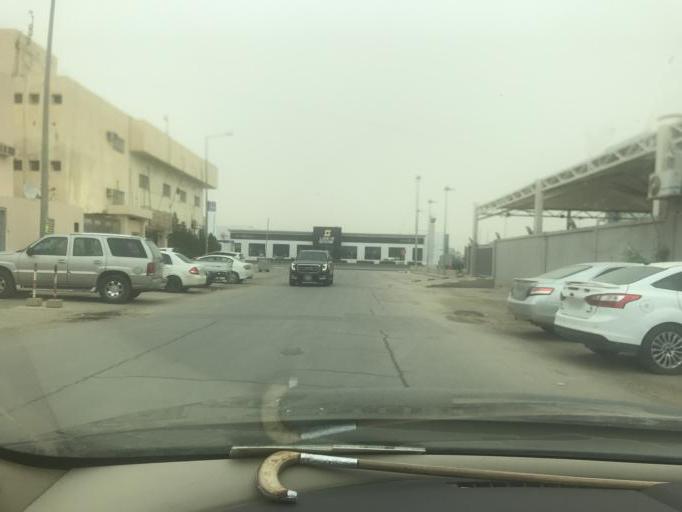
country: SA
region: Ar Riyad
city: Riyadh
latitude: 24.7338
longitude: 46.7904
